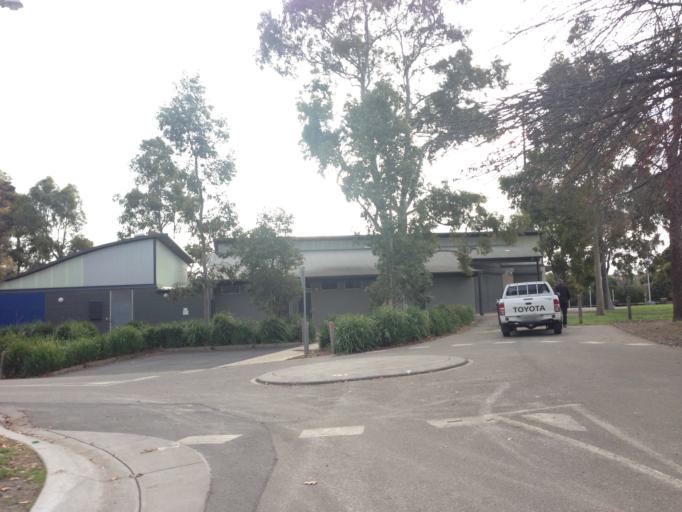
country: AU
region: Victoria
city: Balwyn
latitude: -37.8009
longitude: 145.0739
